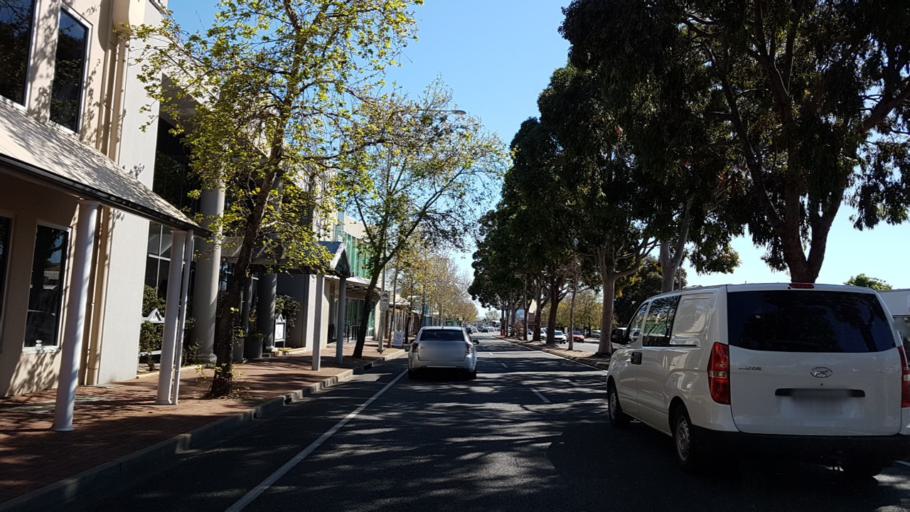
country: AU
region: South Australia
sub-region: City of West Torrens
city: Thebarton
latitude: -34.9237
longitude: 138.5725
